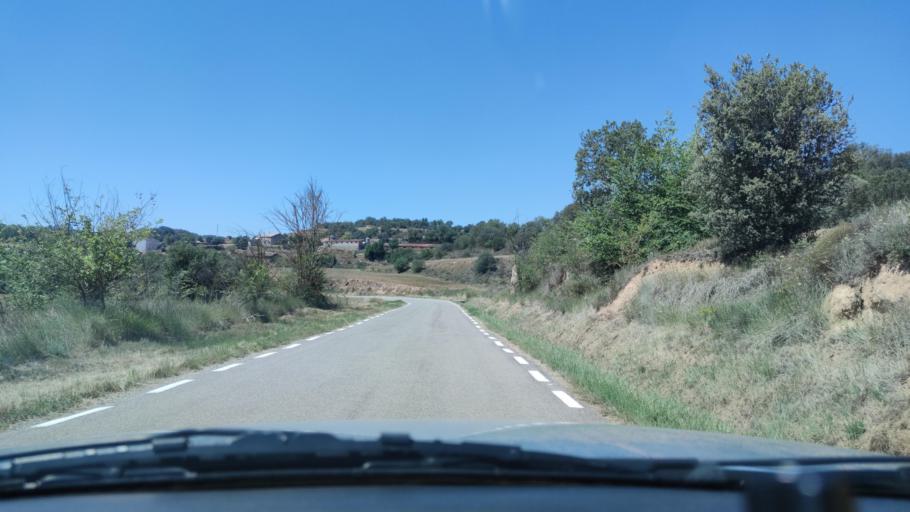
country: ES
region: Catalonia
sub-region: Provincia de Lleida
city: Tora de Riubregos
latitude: 41.8415
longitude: 1.4238
